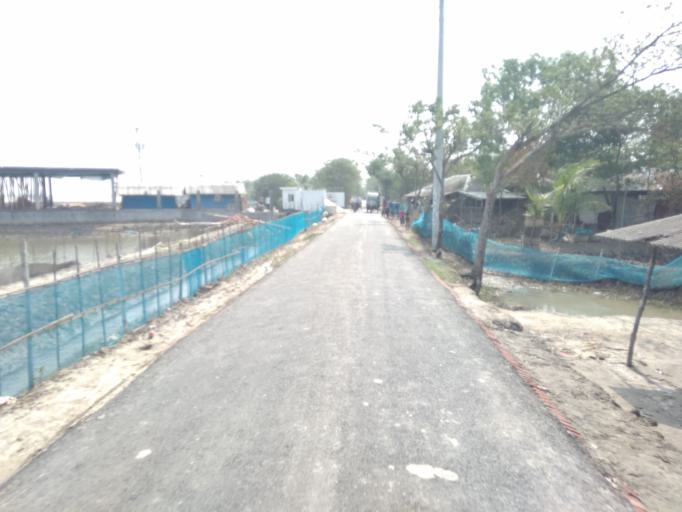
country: IN
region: West Bengal
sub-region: North 24 Parganas
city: Gosaba
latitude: 22.2615
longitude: 89.2240
